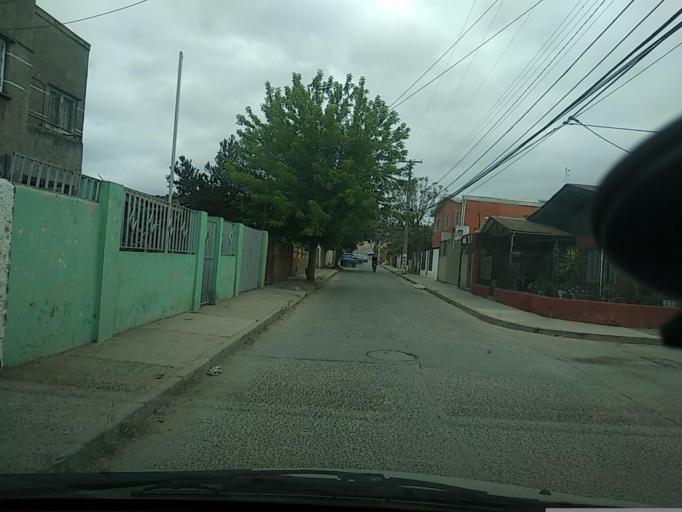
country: CL
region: Valparaiso
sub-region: Provincia de Marga Marga
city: Villa Alemana
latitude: -33.0392
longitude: -71.3601
